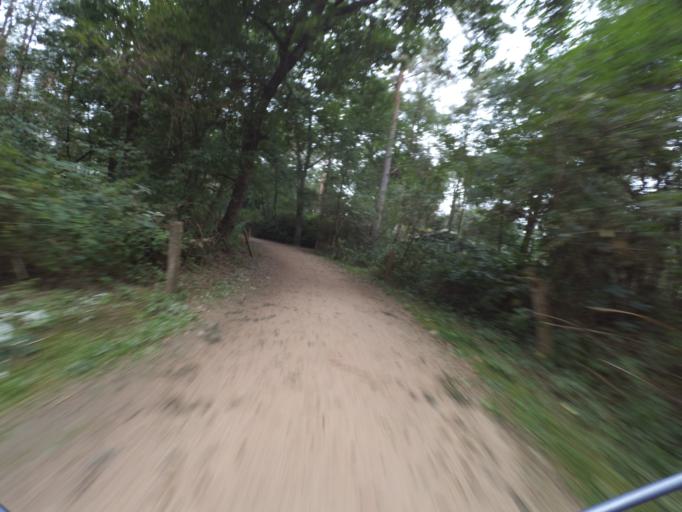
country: NL
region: Overijssel
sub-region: Gemeente Losser
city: Losser
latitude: 52.3301
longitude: 7.0292
